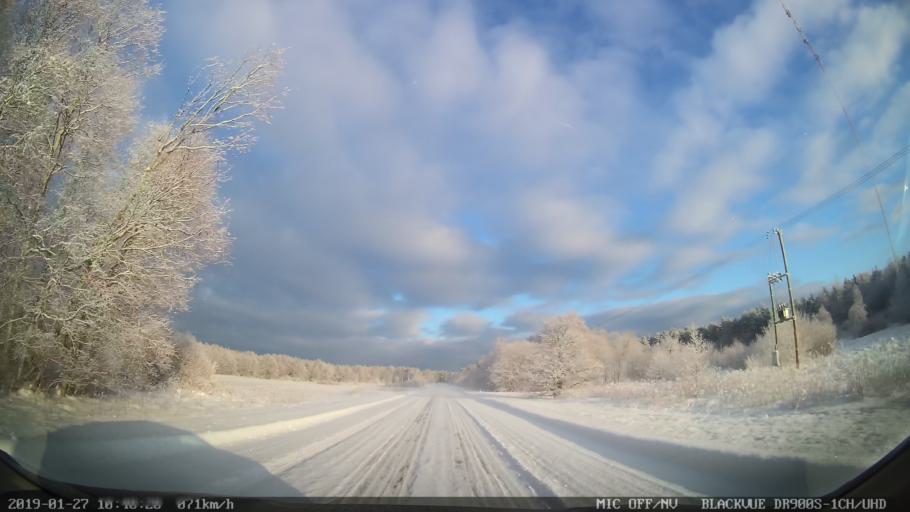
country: EE
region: Harju
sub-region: Raasiku vald
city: Raasiku
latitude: 59.5014
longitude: 25.2612
